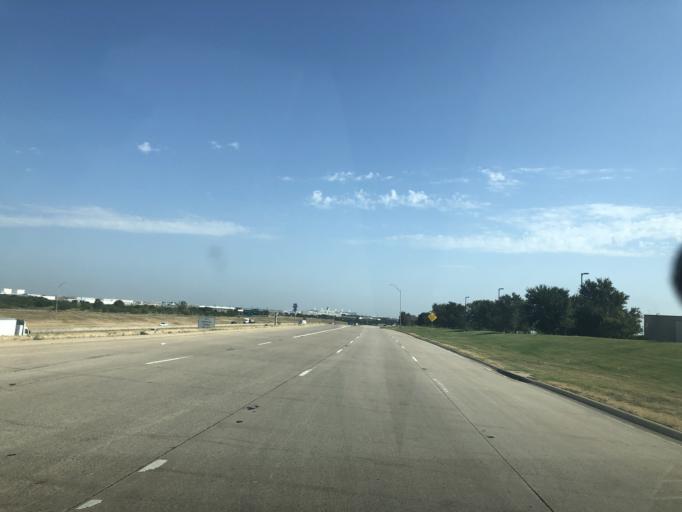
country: US
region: Texas
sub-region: Tarrant County
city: Haslet
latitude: 32.9601
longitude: -97.3097
